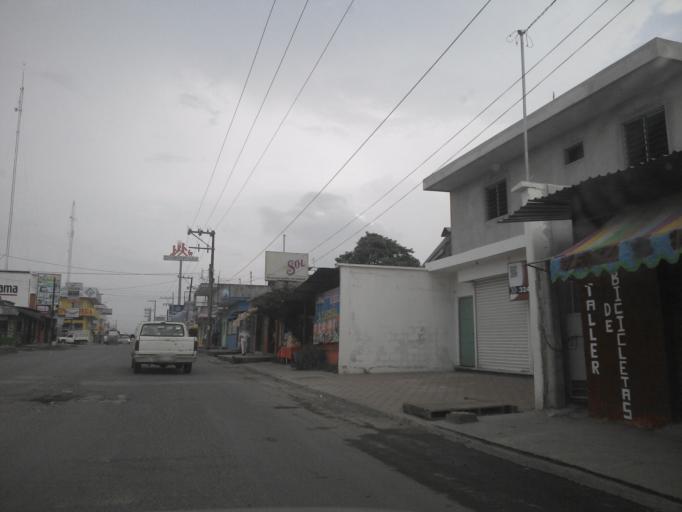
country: MX
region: Veracruz
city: Martinez de la Torre
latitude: 20.0724
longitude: -97.0641
